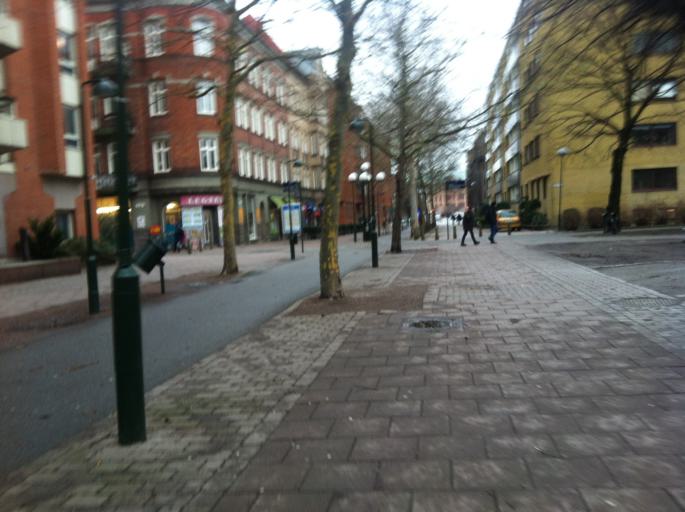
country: SE
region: Skane
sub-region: Malmo
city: Malmoe
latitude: 55.5989
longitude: 13.0060
